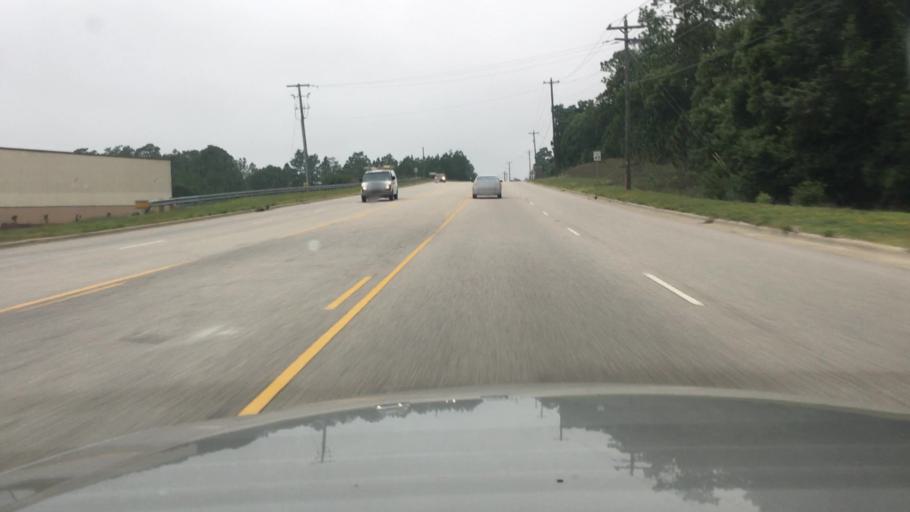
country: US
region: North Carolina
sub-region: Cumberland County
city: Fayetteville
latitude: 35.0112
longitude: -78.8844
